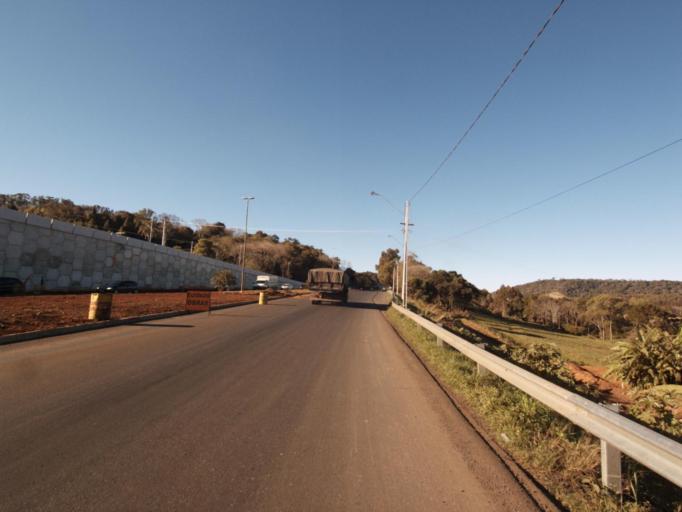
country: BR
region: Santa Catarina
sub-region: Chapeco
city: Chapeco
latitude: -26.9994
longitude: -52.6458
